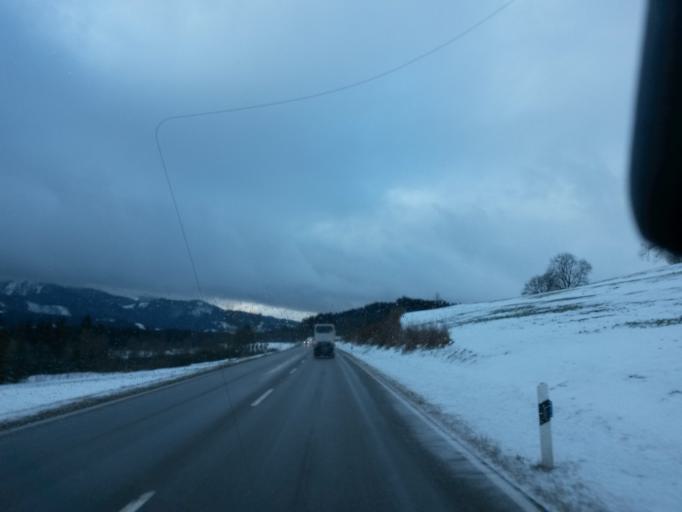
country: DE
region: Bavaria
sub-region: Swabia
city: Oy-Mittelberg
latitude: 47.6249
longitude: 10.4458
